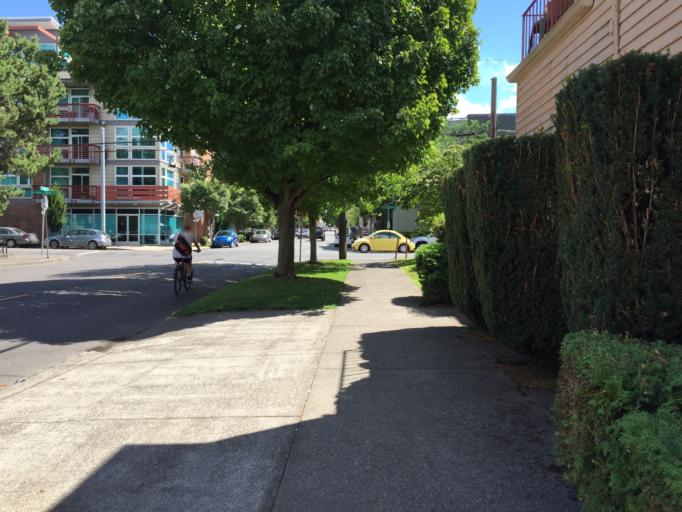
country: US
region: Oregon
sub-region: Multnomah County
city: Portland
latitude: 45.5365
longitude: -122.6235
